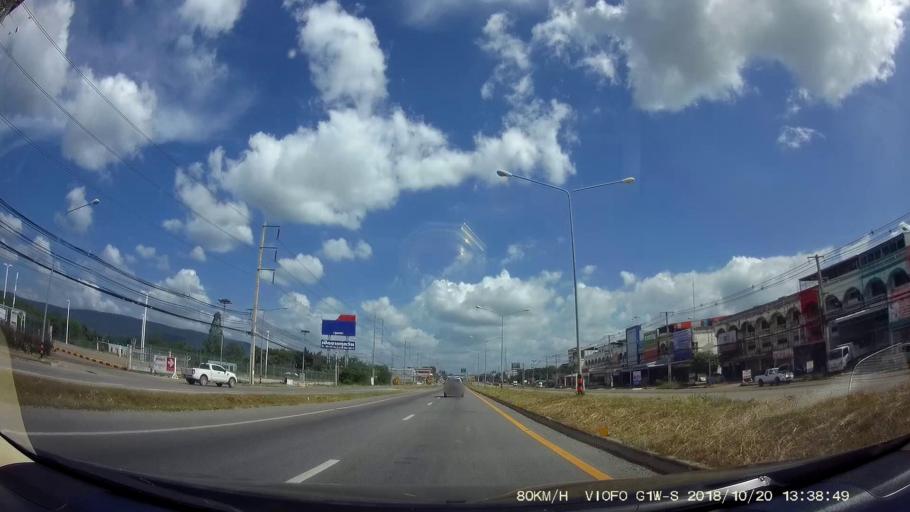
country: TH
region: Khon Kaen
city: Chum Phae
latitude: 16.5511
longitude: 102.0865
